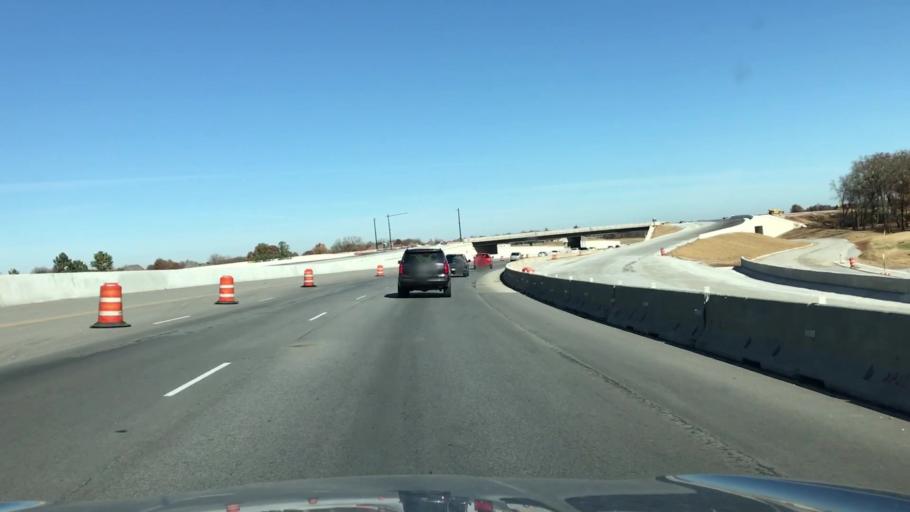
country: US
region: Arkansas
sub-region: Benton County
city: Bentonville
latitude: 36.3613
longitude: -94.1770
